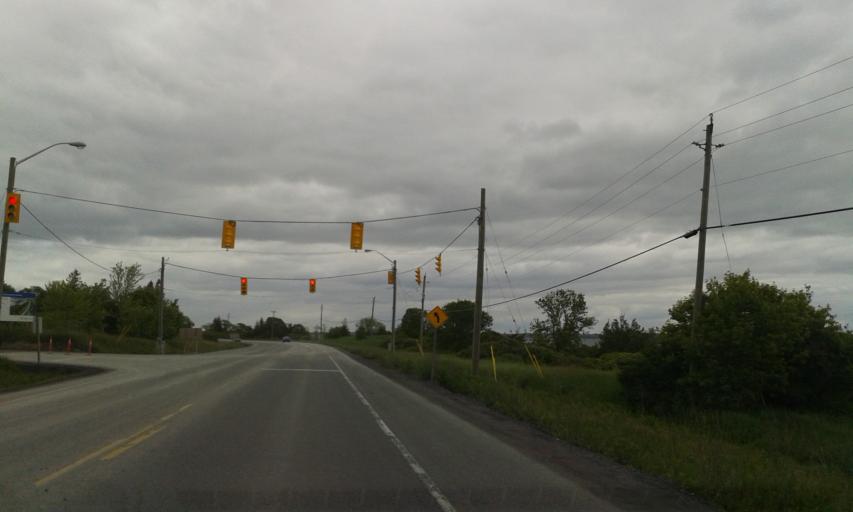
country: CA
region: Ontario
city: Skatepark
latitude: 44.1522
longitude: -76.8319
